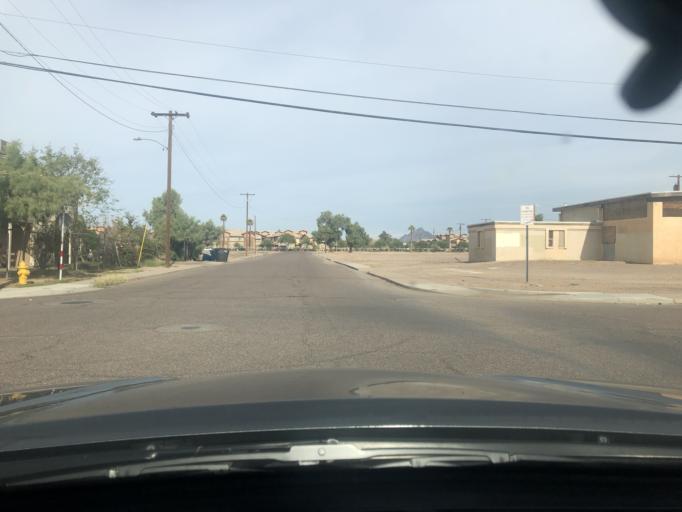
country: US
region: Arizona
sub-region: Maricopa County
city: Phoenix
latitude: 33.4528
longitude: -112.0455
